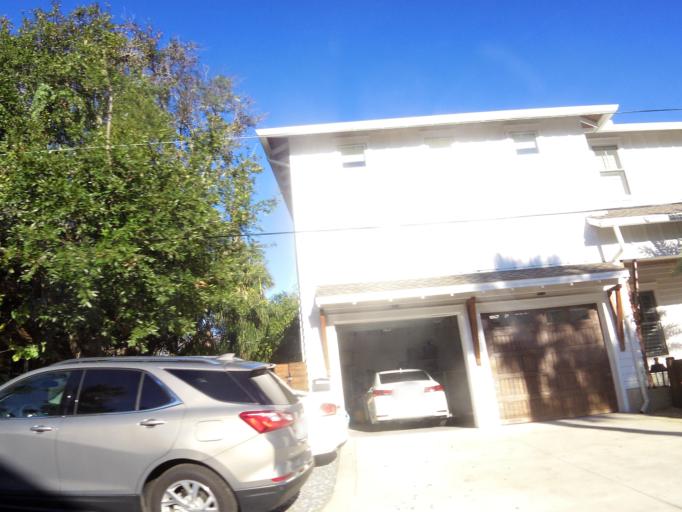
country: US
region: Florida
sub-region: Duval County
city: Atlantic Beach
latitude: 30.3339
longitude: -81.3984
